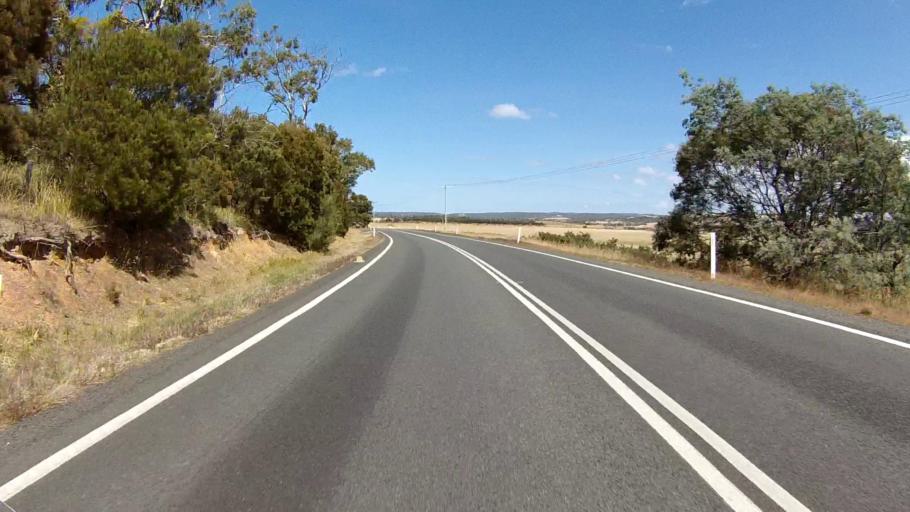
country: AU
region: Tasmania
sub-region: Break O'Day
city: St Helens
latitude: -42.0846
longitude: 148.0661
